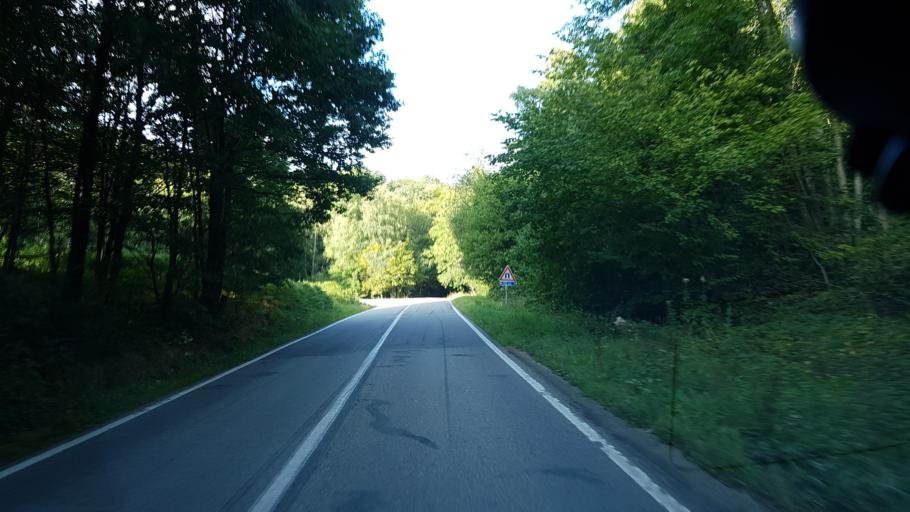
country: BE
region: Wallonia
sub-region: Province de Liege
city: Theux
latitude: 50.4908
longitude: 5.8186
